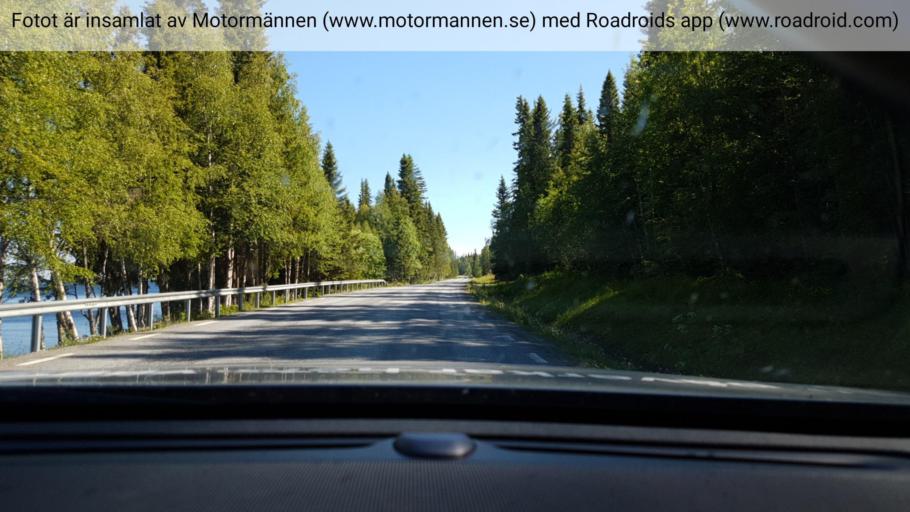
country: SE
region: Vaesterbotten
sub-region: Vilhelmina Kommun
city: Sjoberg
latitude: 64.6639
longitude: 16.3079
